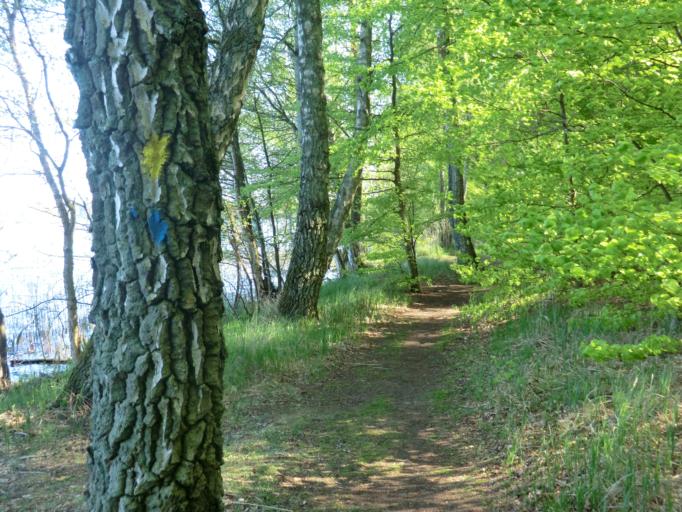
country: SE
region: Skane
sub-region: Sjobo Kommun
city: Sjoebo
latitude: 55.5706
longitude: 13.7183
